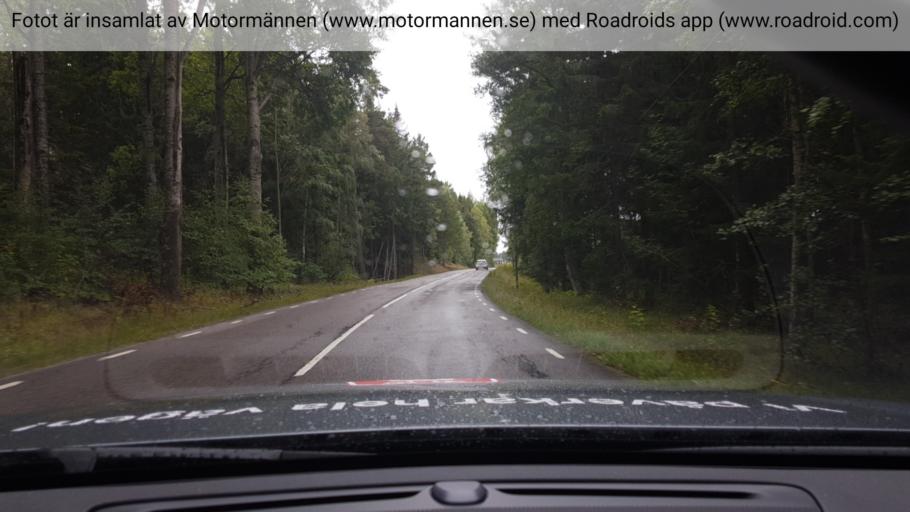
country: SE
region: Stockholm
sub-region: Botkyrka Kommun
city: Varsta
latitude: 59.1160
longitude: 17.8584
